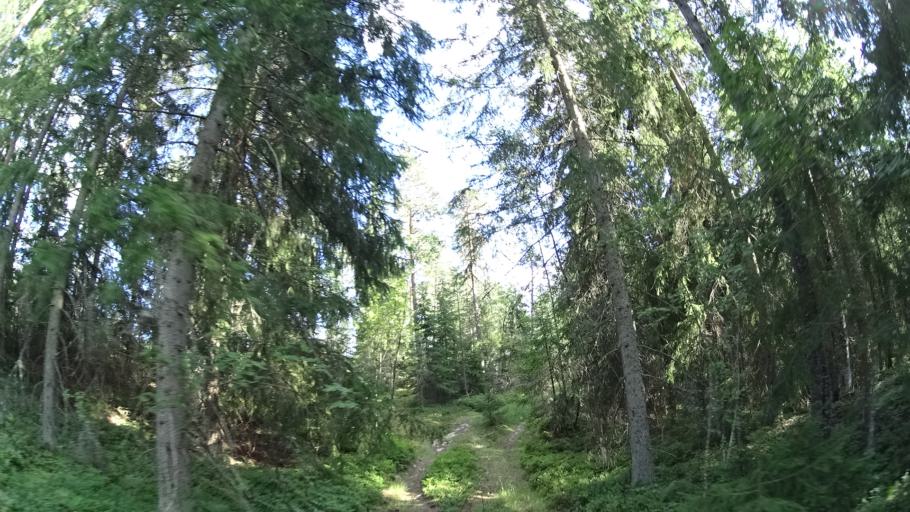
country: FI
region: Uusimaa
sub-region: Helsinki
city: Vihti
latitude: 60.3737
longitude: 24.3630
